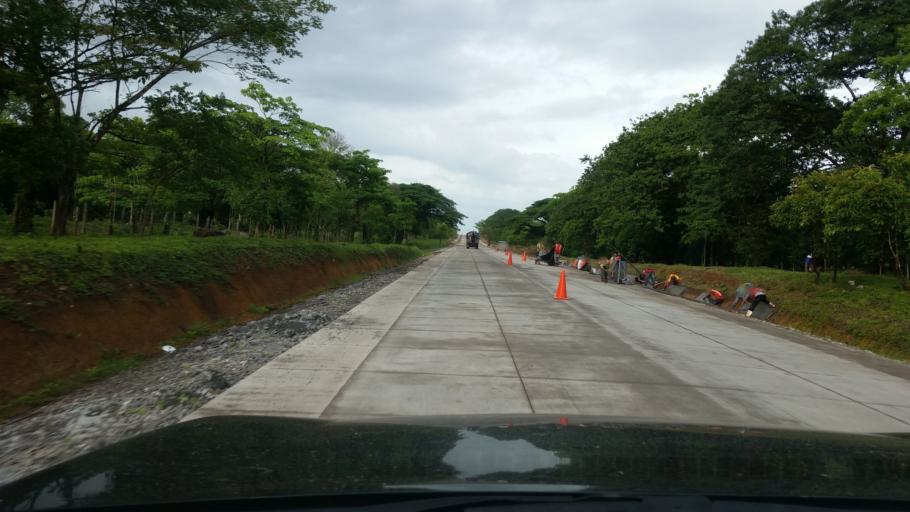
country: NI
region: Matagalpa
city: Rio Blanco
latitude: 13.1342
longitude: -85.0354
